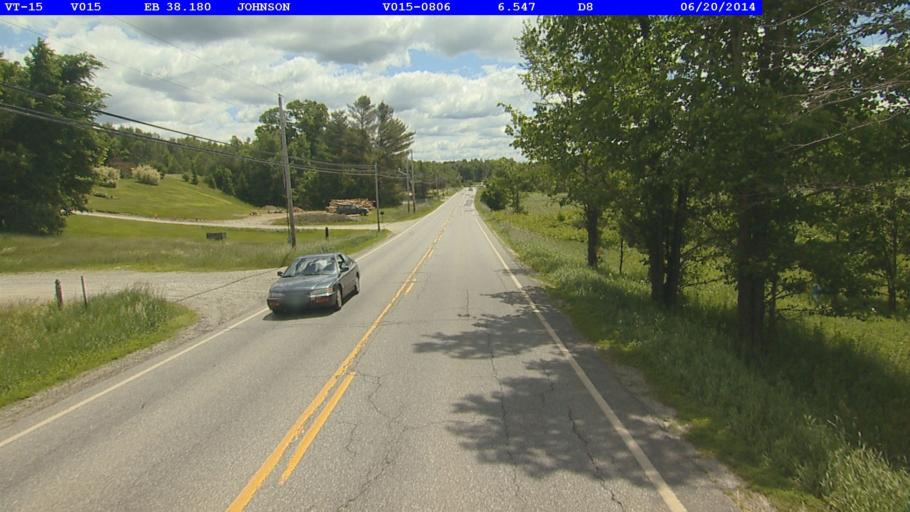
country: US
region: Vermont
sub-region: Lamoille County
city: Johnson
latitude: 44.6112
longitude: -72.6516
